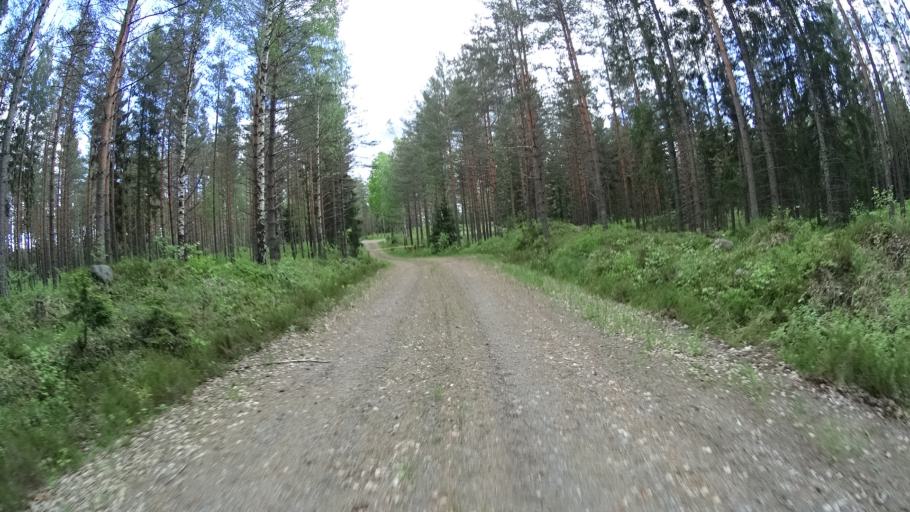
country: FI
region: Uusimaa
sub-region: Raaseporin
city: Pohja
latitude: 60.1811
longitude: 23.5568
